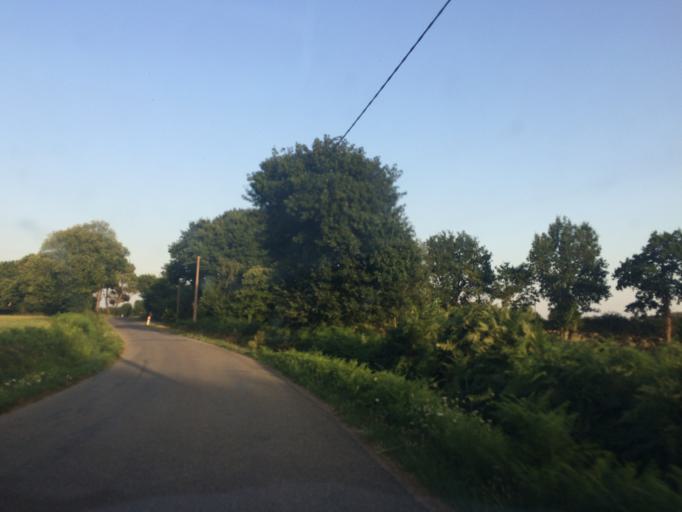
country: FR
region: Brittany
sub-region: Departement du Morbihan
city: Allaire
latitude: 47.6359
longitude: -2.2087
